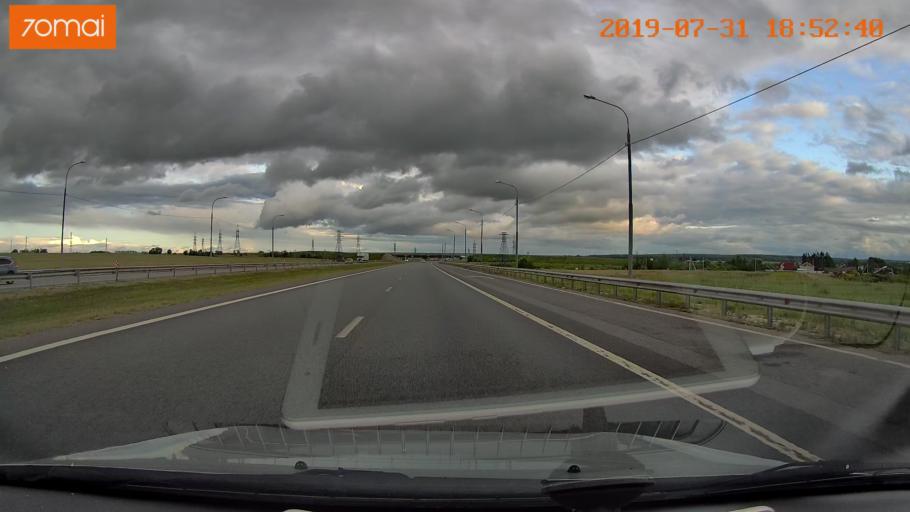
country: RU
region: Moskovskaya
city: Voskresensk
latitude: 55.2114
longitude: 38.6372
